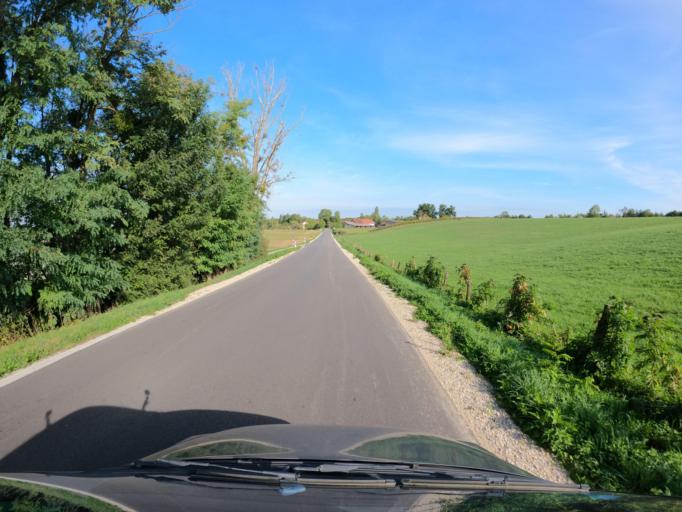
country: FR
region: Franche-Comte
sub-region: Departement du Jura
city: Bletterans
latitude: 46.7344
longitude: 5.5030
